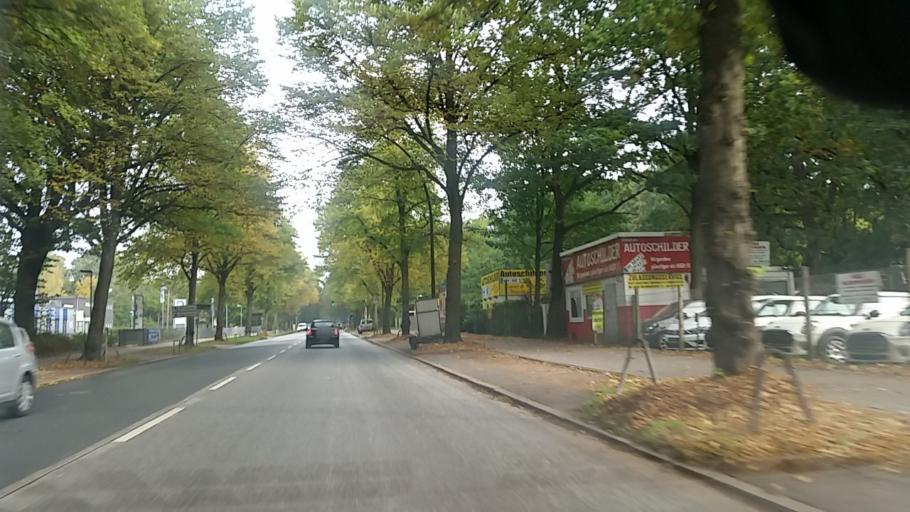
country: DE
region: Hamburg
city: Langenhorn
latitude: 53.6671
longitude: 10.0018
